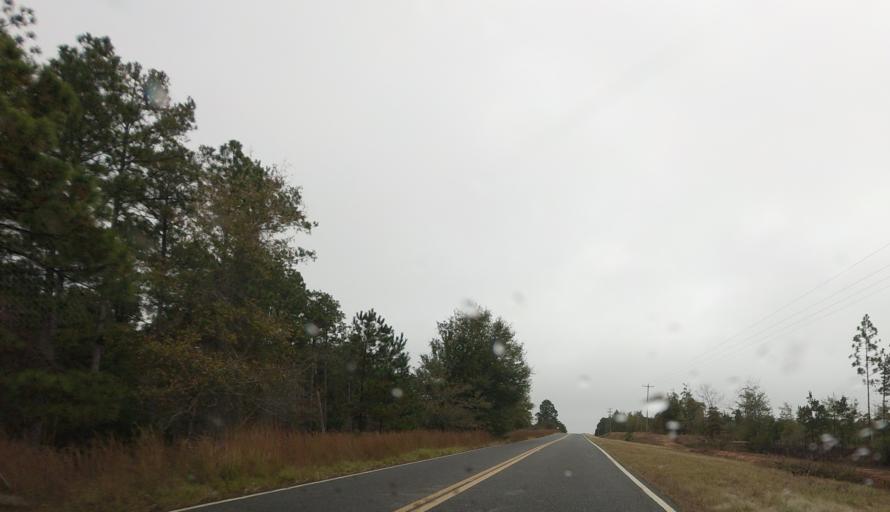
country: US
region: Georgia
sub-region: Taylor County
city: Butler
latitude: 32.4390
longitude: -84.3622
